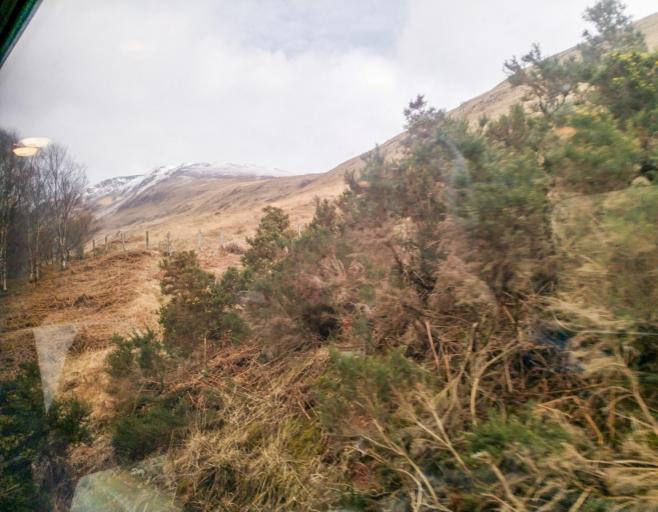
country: GB
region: Scotland
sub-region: Highland
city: Spean Bridge
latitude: 56.8083
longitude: -4.7182
